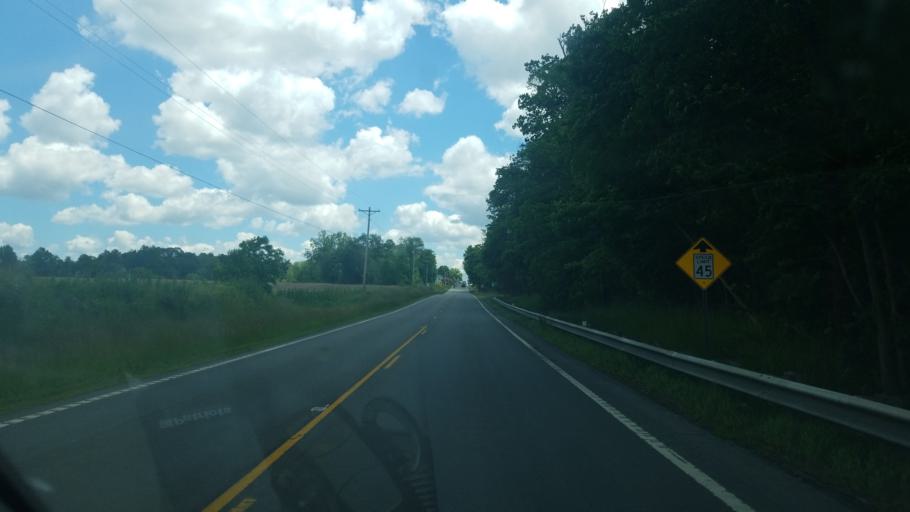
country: US
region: Ohio
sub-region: Huron County
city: New London
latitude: 41.0294
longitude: -82.3984
